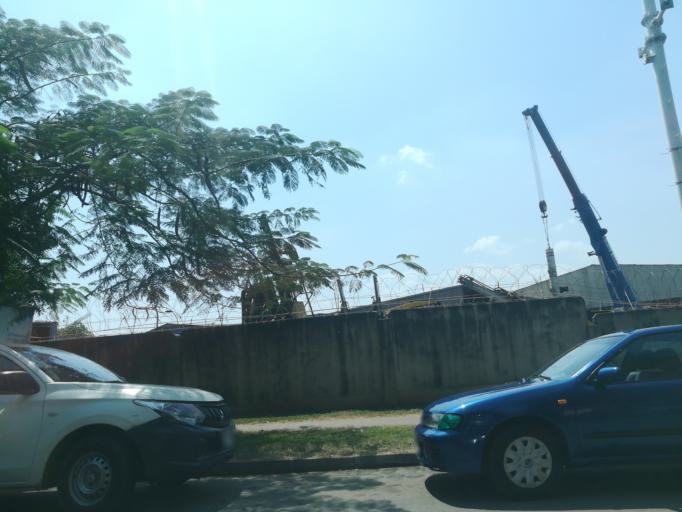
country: NG
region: Abuja Federal Capital Territory
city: Abuja
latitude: 9.0645
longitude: 7.4478
